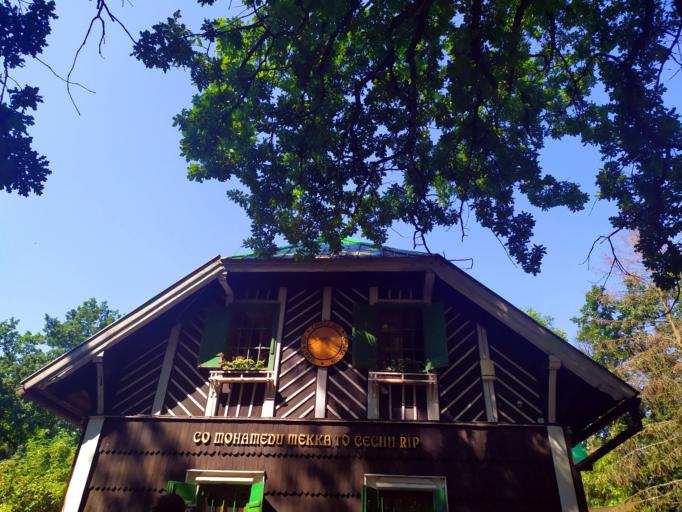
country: CZ
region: Ustecky
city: Roudnice nad Labem
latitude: 50.3856
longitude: 14.2892
